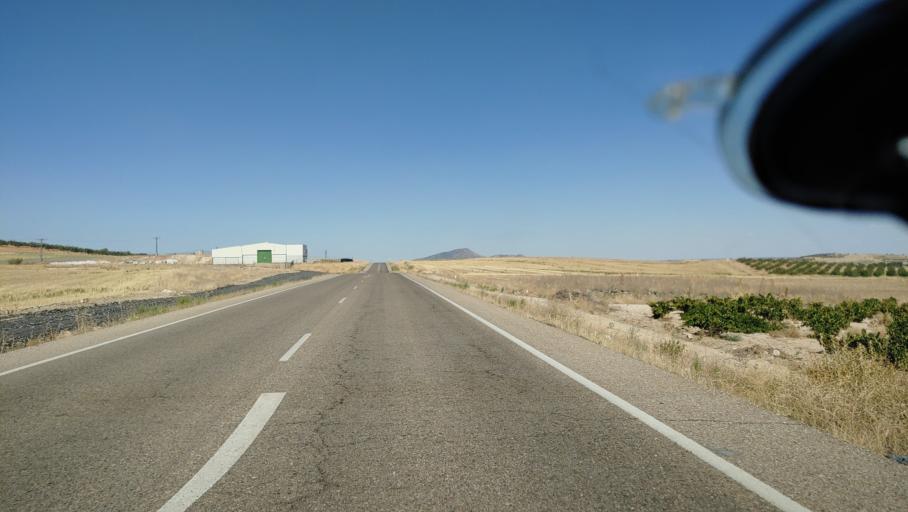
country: ES
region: Castille-La Mancha
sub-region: Province of Toledo
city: Pulgar
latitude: 39.6788
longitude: -4.1793
